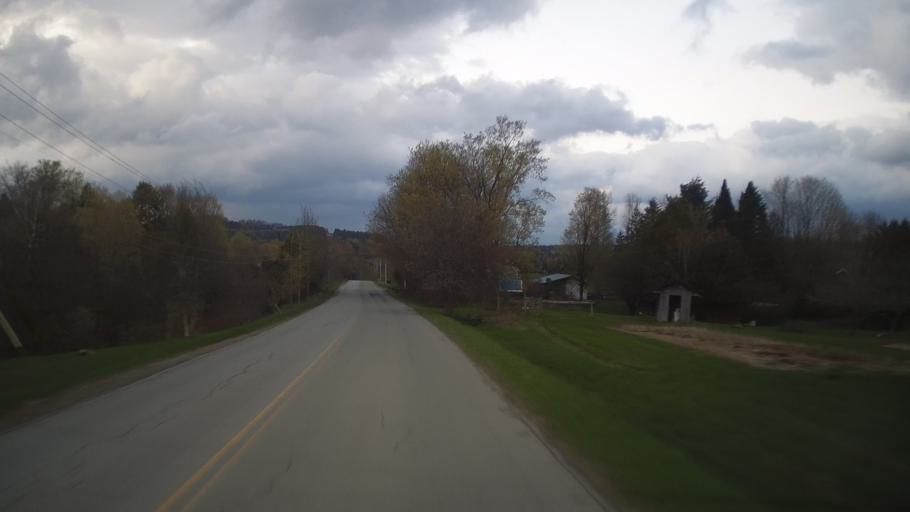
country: US
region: Vermont
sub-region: Orleans County
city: Newport
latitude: 44.7322
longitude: -72.2228
